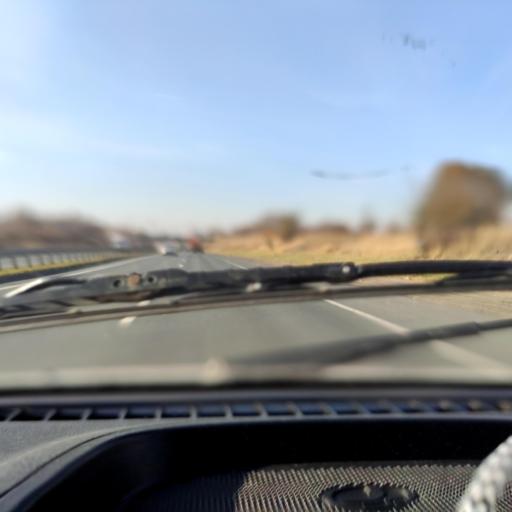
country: RU
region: Samara
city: Tol'yatti
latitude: 53.5680
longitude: 49.4878
